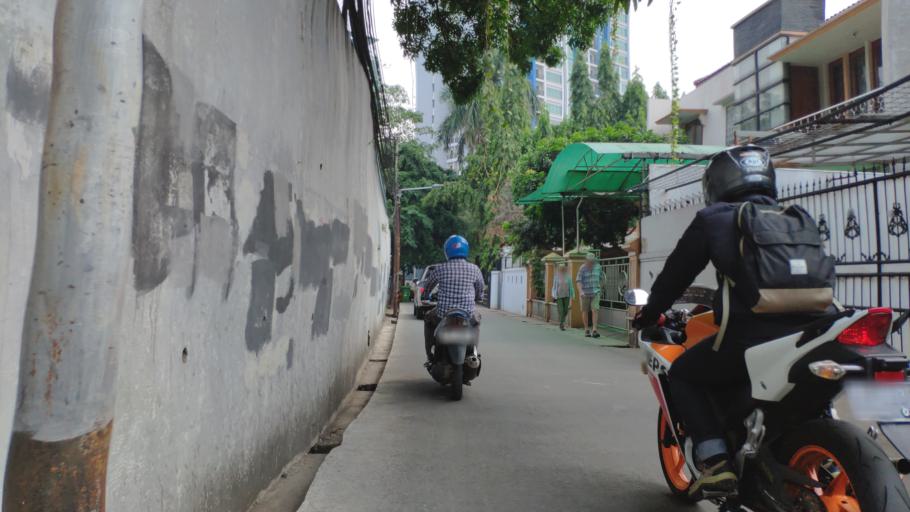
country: ID
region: Banten
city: South Tangerang
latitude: -6.2840
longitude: 106.7903
